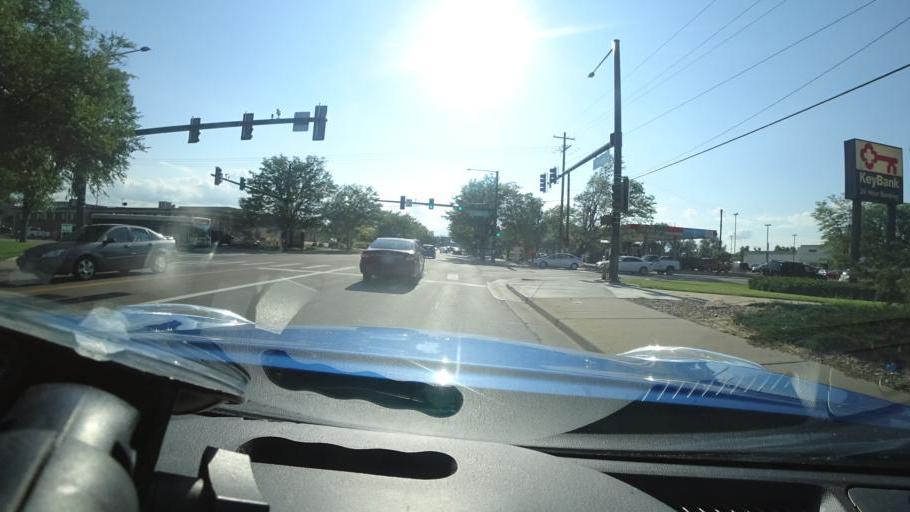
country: US
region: Colorado
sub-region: Arapahoe County
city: Sheridan
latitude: 39.6787
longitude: -105.0200
